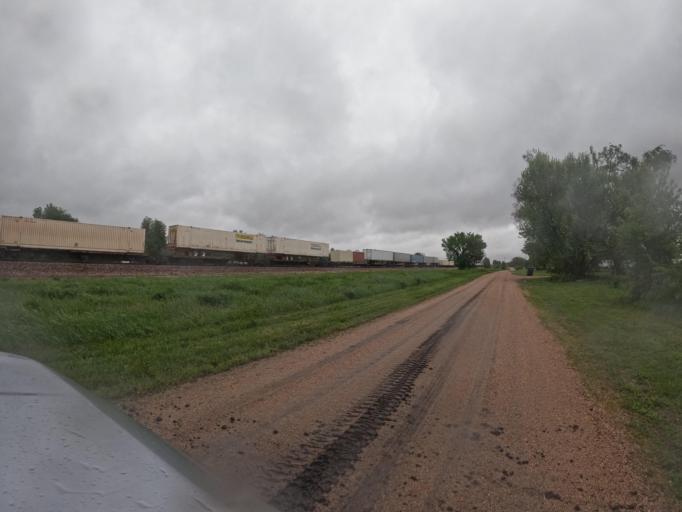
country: US
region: Nebraska
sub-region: Clay County
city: Harvard
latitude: 40.6165
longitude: -98.1022
